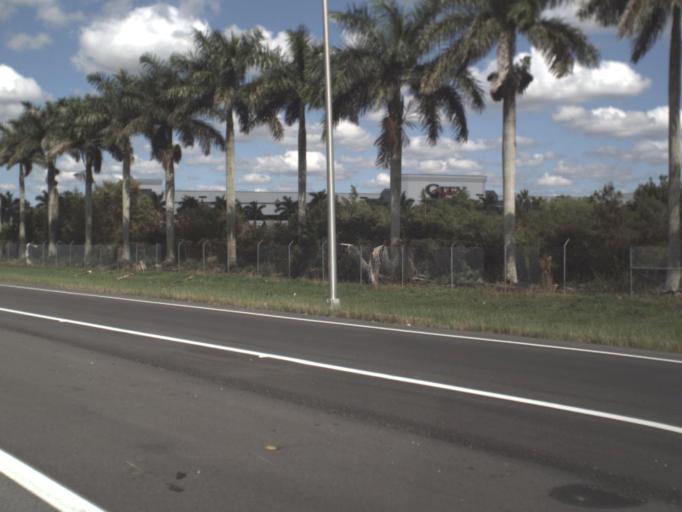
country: US
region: Florida
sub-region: Broward County
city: Tamarac
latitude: 26.1991
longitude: -80.2955
